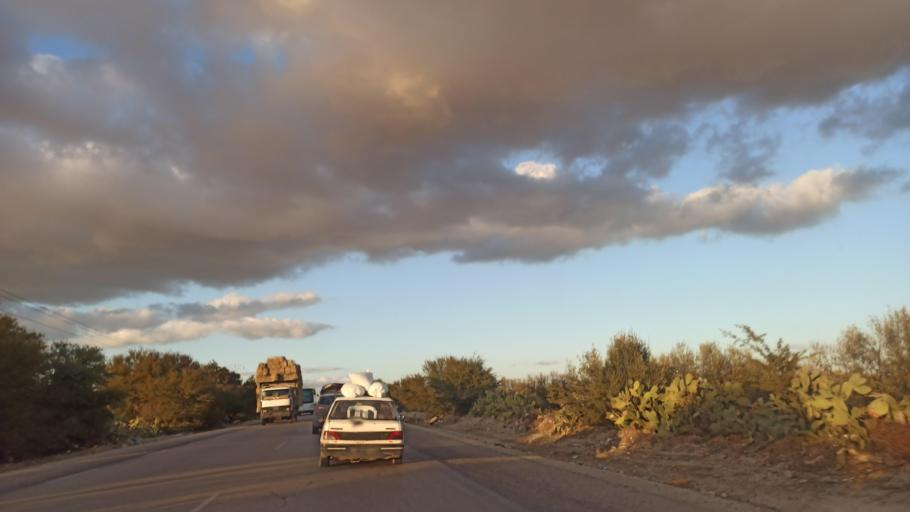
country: TN
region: Susah
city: Sidi Bou Ali
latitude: 36.0152
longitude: 10.3190
